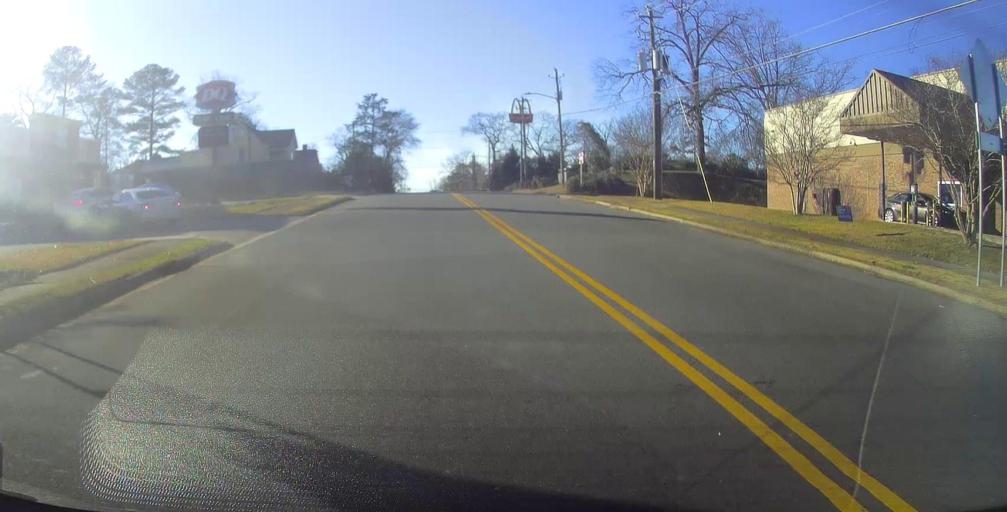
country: US
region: Georgia
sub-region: Meriwether County
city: Manchester
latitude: 32.8529
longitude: -84.6179
